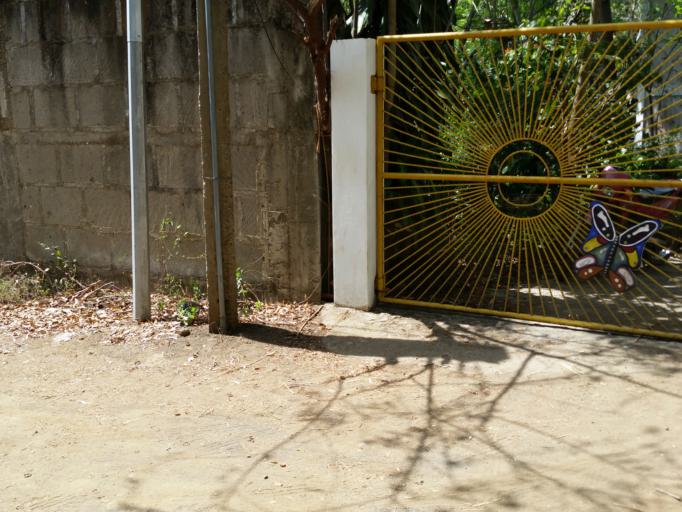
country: NI
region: Masaya
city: La Concepcion
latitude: 11.9500
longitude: -86.1824
